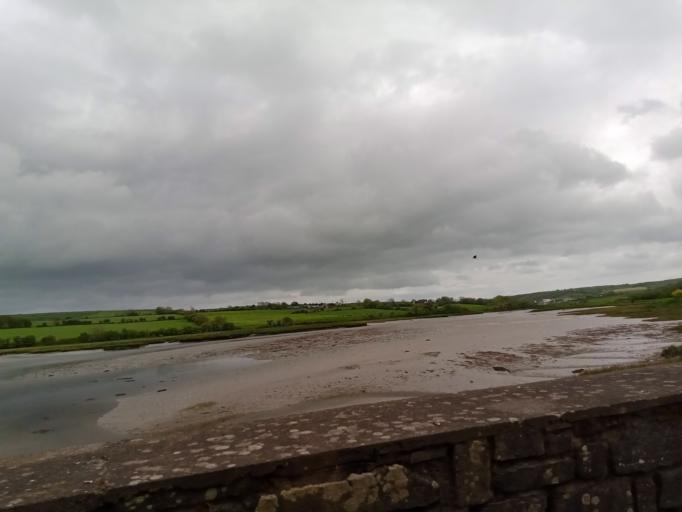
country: IE
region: Munster
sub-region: County Cork
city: Bandon
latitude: 51.6421
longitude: -8.7643
